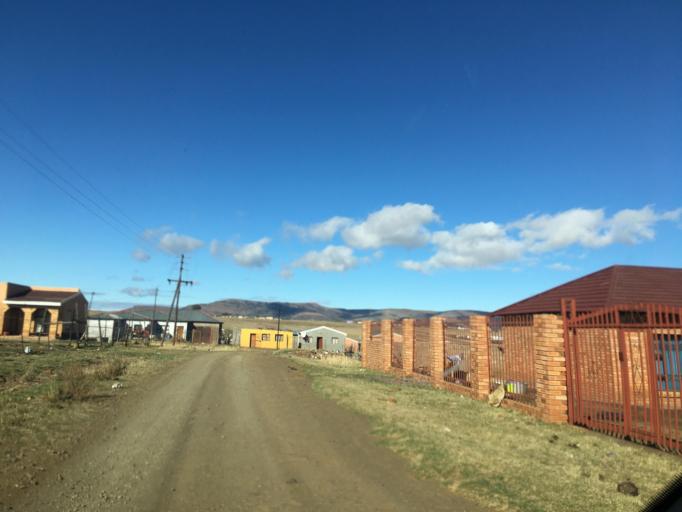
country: ZA
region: Eastern Cape
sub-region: Chris Hani District Municipality
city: Cala
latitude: -31.5390
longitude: 27.6939
